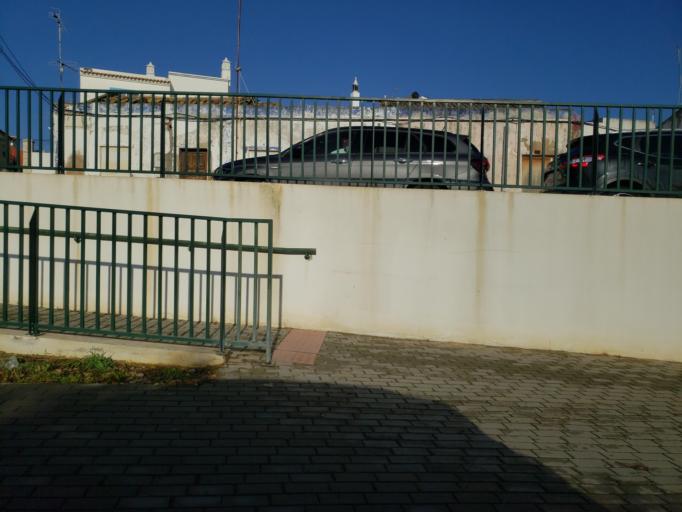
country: PT
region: Faro
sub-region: Portimao
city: Portimao
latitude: 37.1494
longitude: -8.5506
